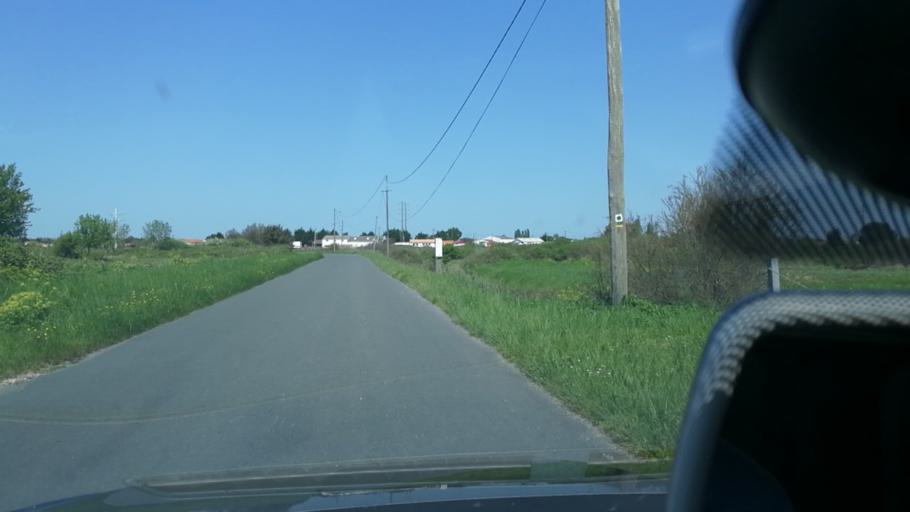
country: FR
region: Poitou-Charentes
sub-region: Departement de la Charente-Maritime
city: Saint-Trojan-les-Bains
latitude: 45.8676
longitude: -1.2204
